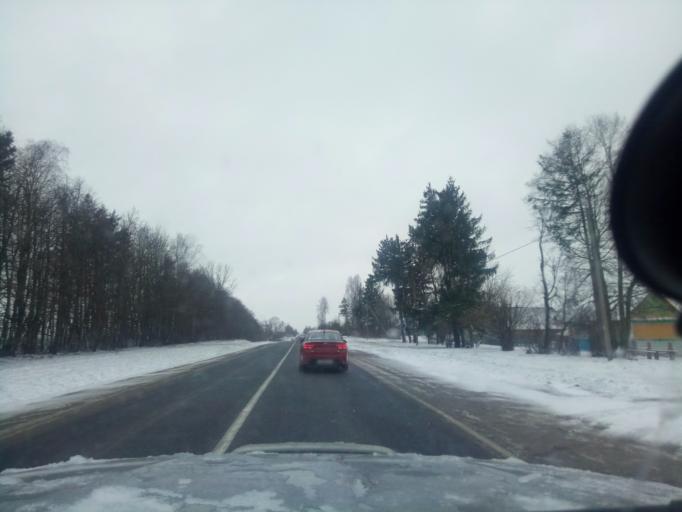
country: BY
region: Minsk
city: Klyetsk
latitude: 53.1342
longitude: 26.6742
